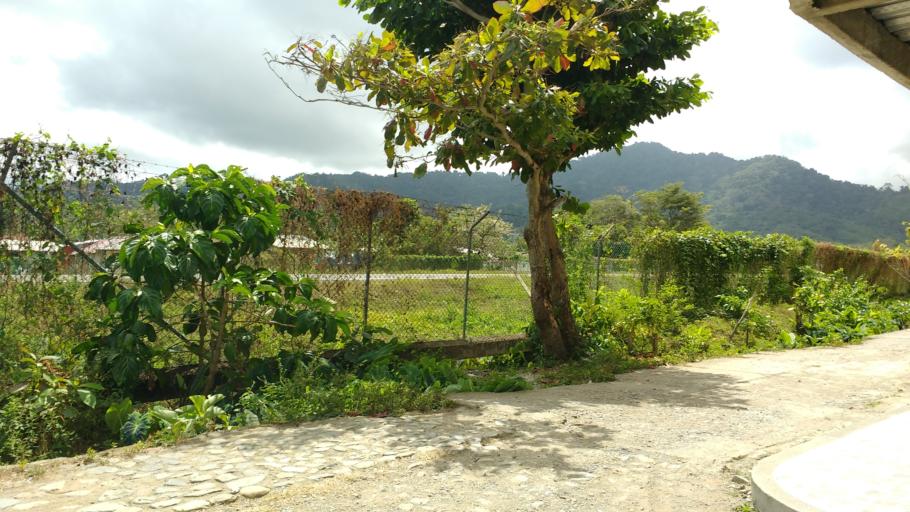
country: PA
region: Guna Yala
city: Puerto Obaldia
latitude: 8.6346
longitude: -77.3490
